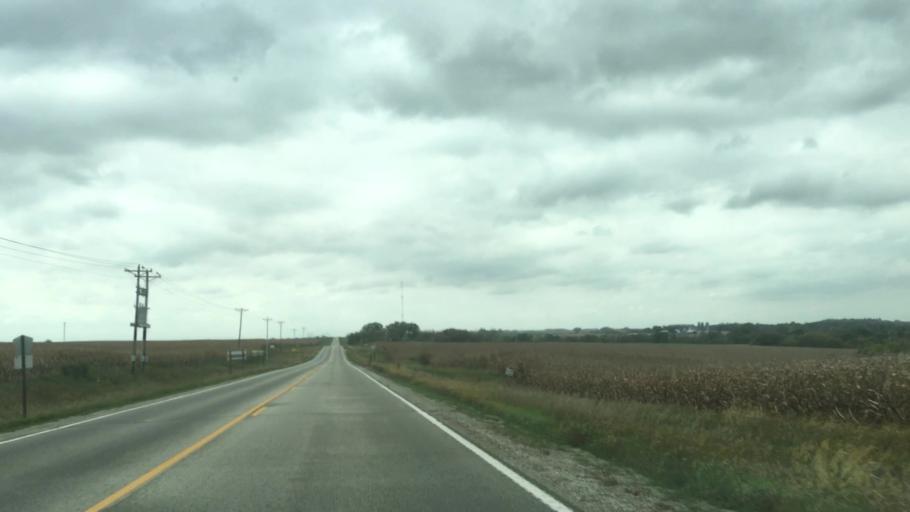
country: US
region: Minnesota
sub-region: Fillmore County
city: Preston
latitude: 43.7319
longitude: -92.0606
